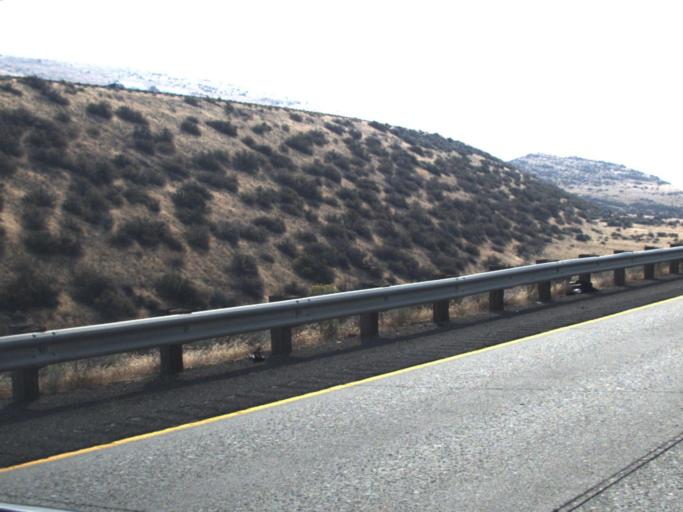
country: US
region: Washington
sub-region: Kittitas County
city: Kittitas
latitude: 46.8734
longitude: -120.4220
